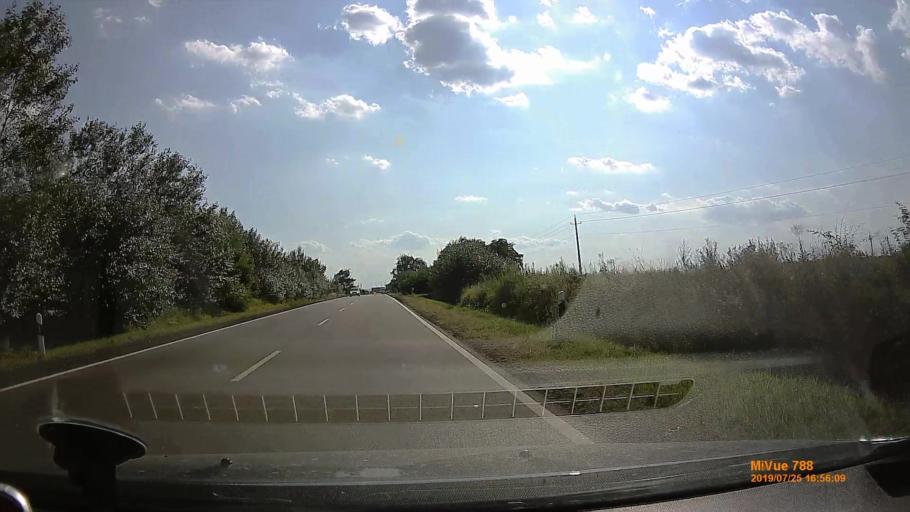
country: HU
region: Heves
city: Hatvan
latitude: 47.6711
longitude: 19.7271
